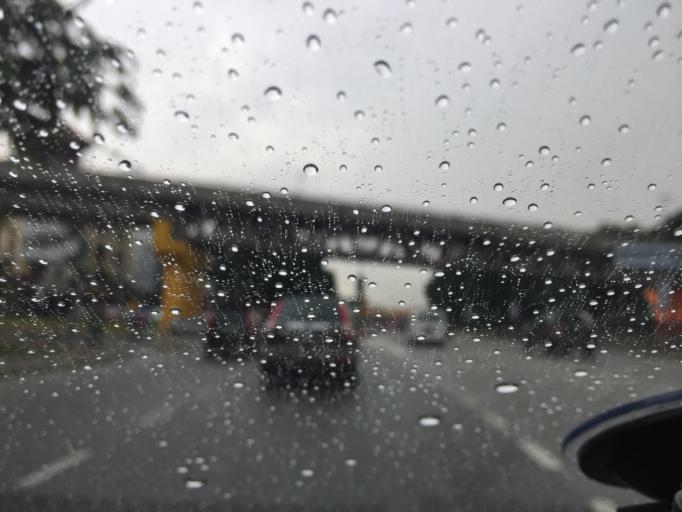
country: MY
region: Selangor
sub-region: Petaling
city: Petaling Jaya
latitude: 3.0742
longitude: 101.6094
